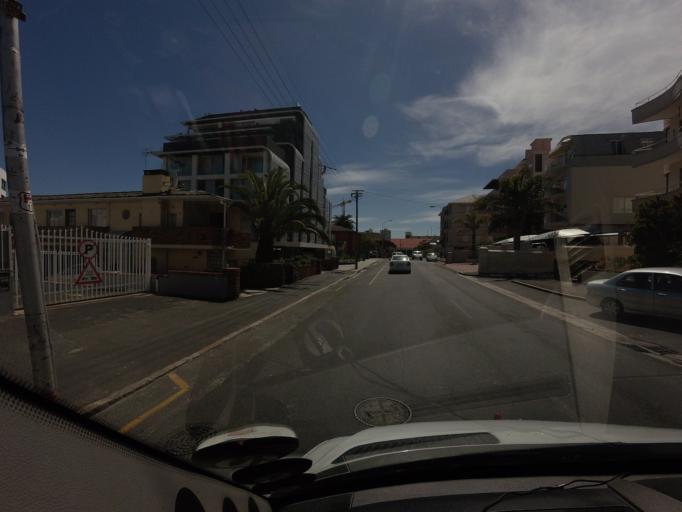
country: ZA
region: Western Cape
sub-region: City of Cape Town
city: Cape Town
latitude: -33.9240
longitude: 18.3800
